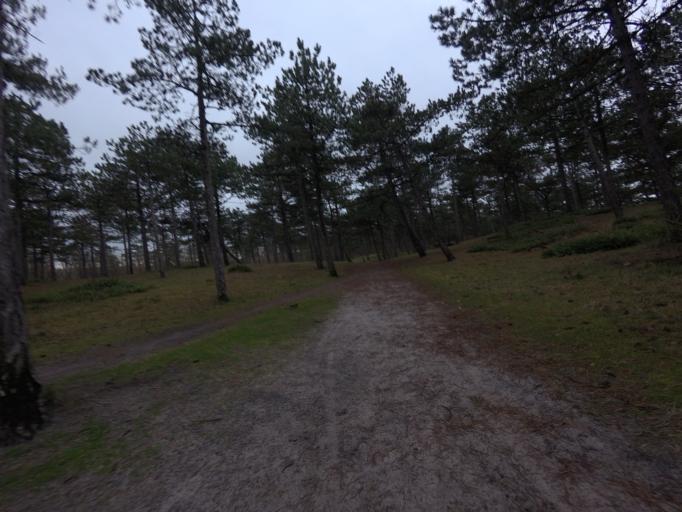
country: NL
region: North Holland
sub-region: Gemeente Texel
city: Den Burg
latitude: 53.0937
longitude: 4.7566
